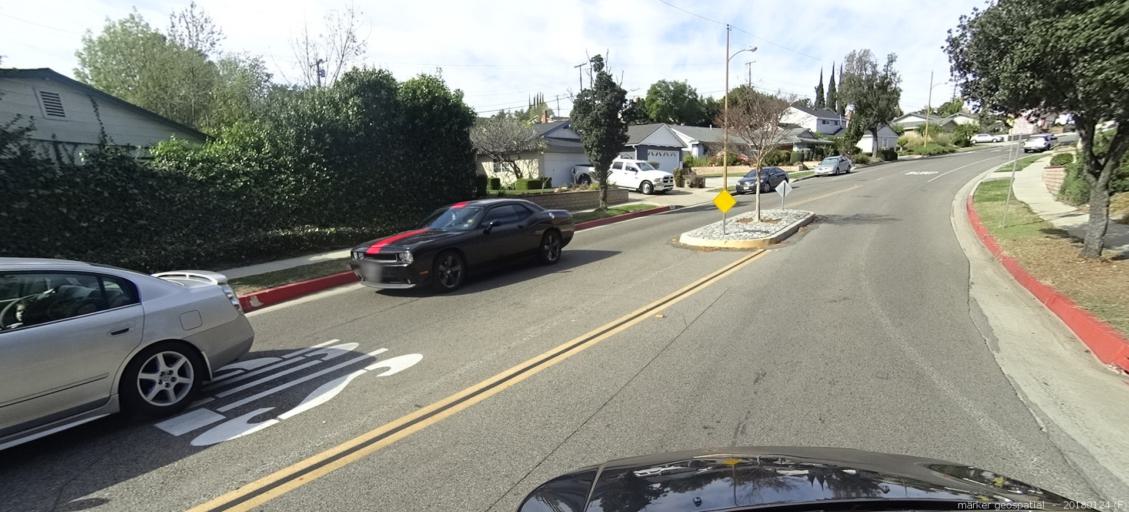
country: US
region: California
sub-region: Los Angeles County
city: Diamond Bar
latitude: 34.0228
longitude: -117.8166
